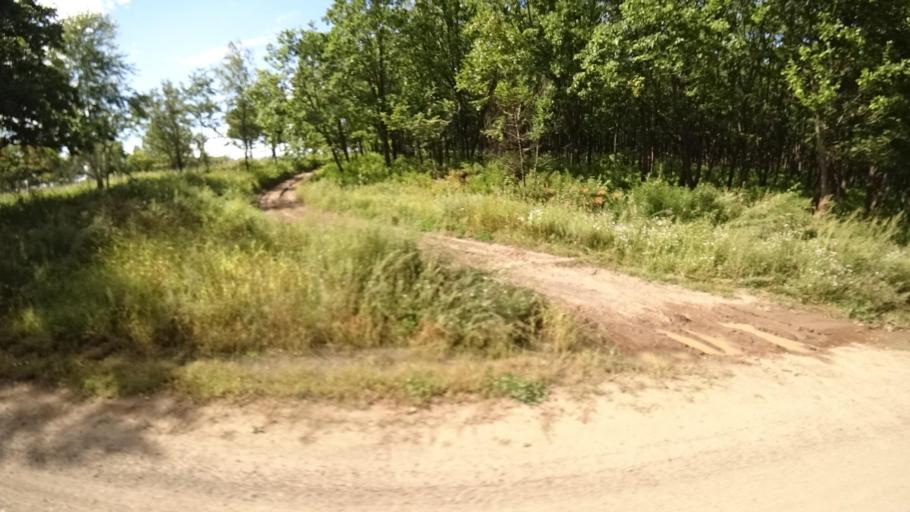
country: RU
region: Primorskiy
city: Yakovlevka
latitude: 44.3840
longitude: 133.5359
